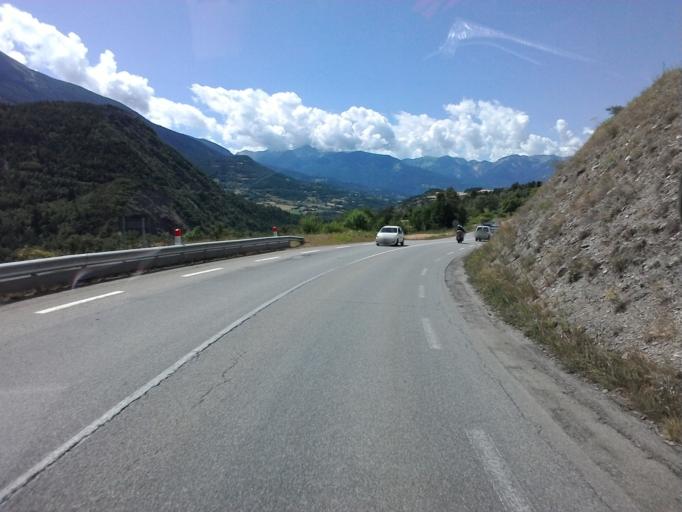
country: FR
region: Provence-Alpes-Cote d'Azur
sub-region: Departement des Hautes-Alpes
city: Embrun
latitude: 44.6300
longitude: 6.5474
